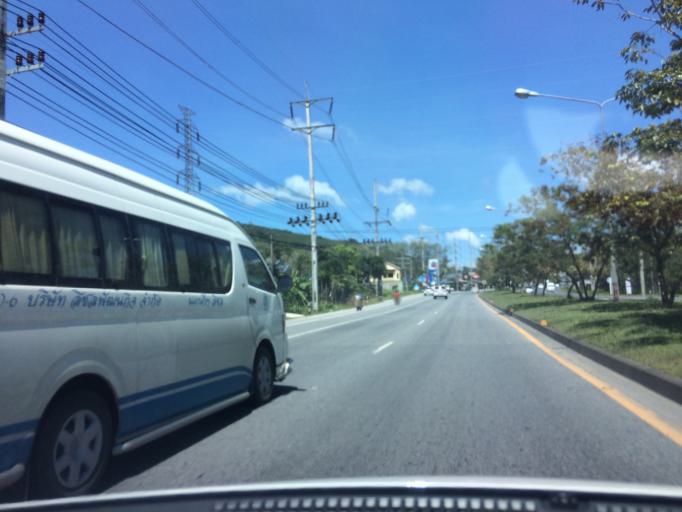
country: TH
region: Phuket
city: Thalang
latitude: 8.1211
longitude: 98.3361
